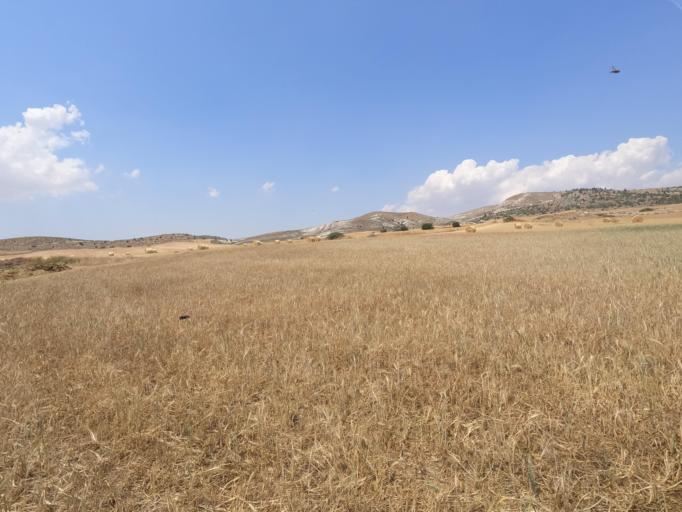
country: CY
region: Larnaka
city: Voroklini
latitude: 35.0081
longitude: 33.6517
